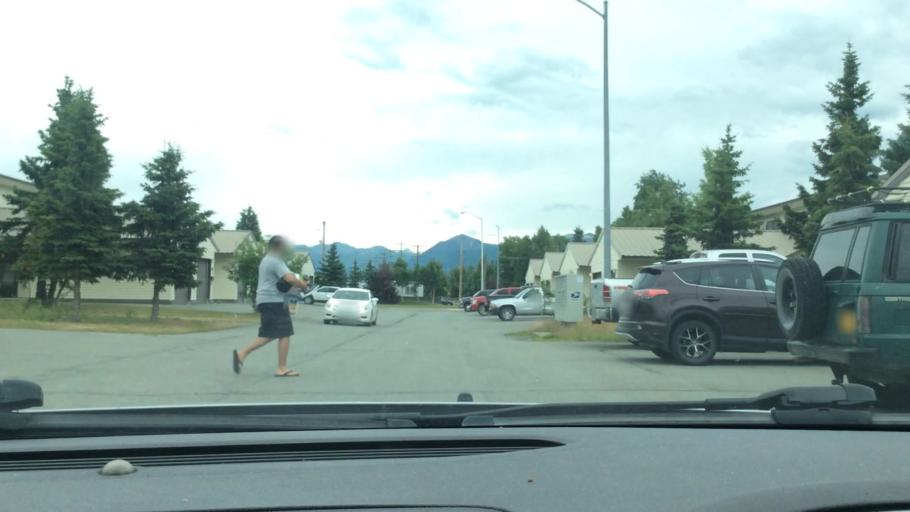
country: US
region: Alaska
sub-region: Anchorage Municipality
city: Anchorage
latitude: 61.2303
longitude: -149.8503
